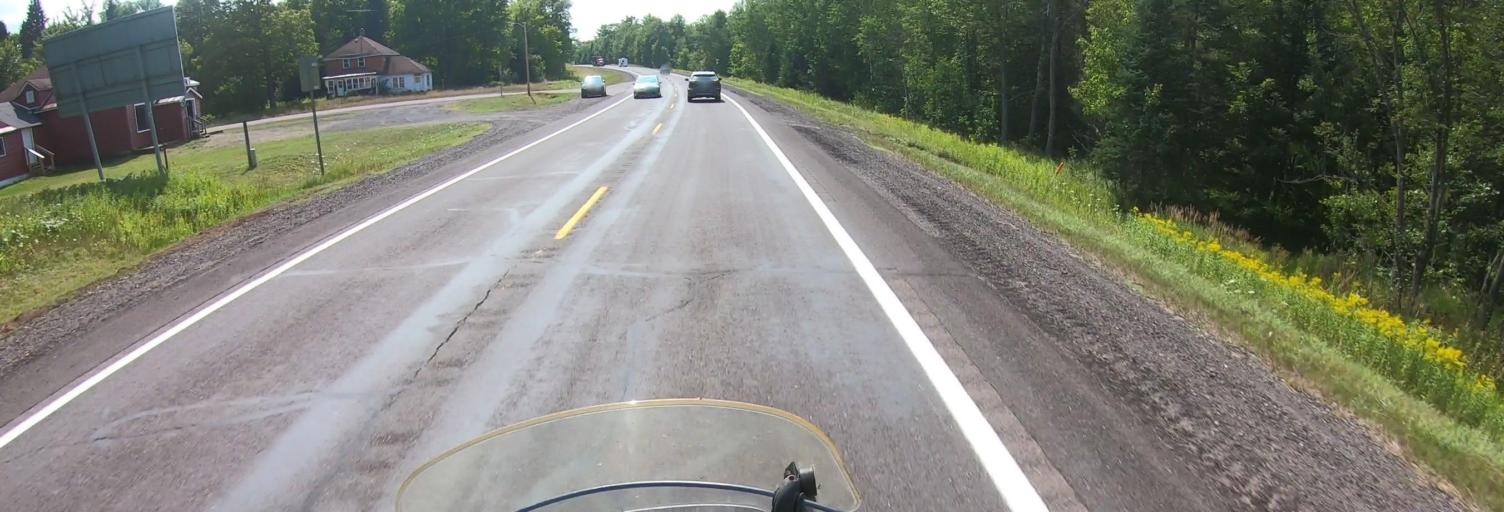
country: US
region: Michigan
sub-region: Houghton County
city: Hancock
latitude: 46.8697
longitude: -88.8945
